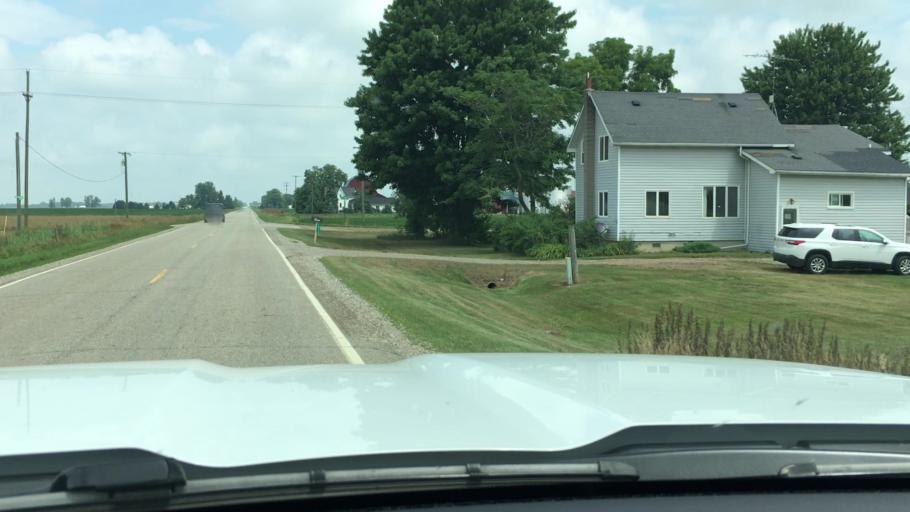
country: US
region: Michigan
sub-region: Sanilac County
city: Marlette
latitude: 43.3869
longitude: -83.0069
